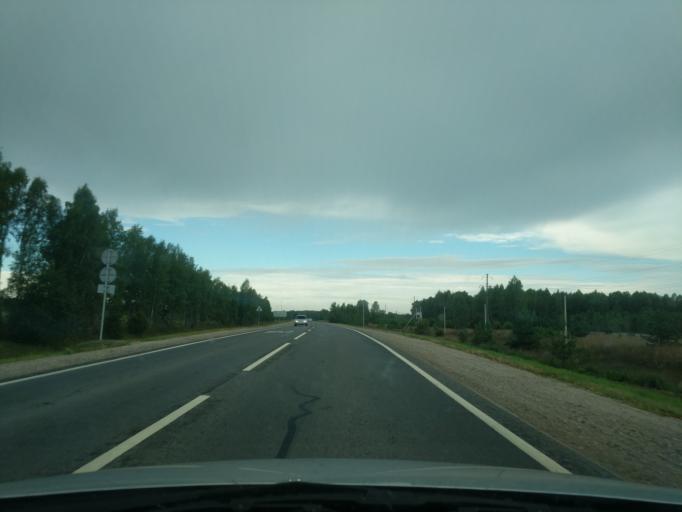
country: RU
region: Kostroma
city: Ostrovskoye
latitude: 57.8085
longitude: 42.2875
